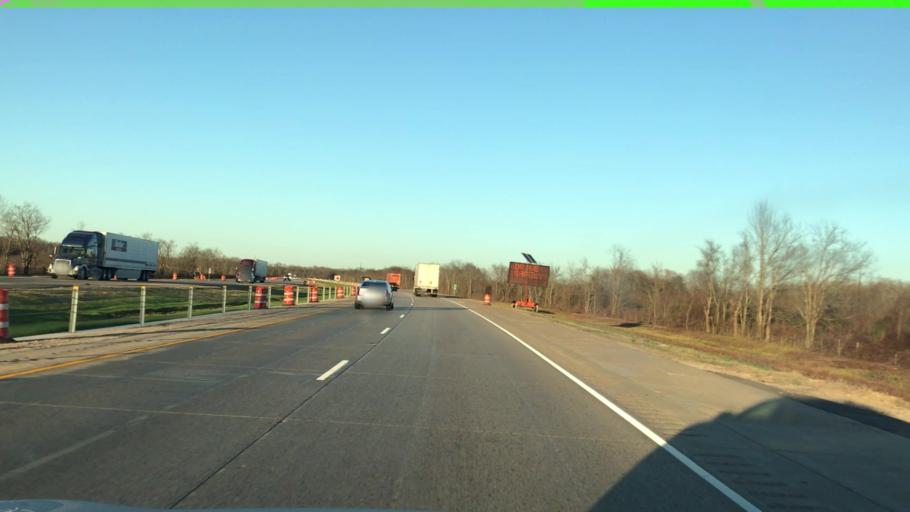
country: US
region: Arkansas
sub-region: Miller County
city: Texarkana
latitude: 33.5742
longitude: -93.8473
